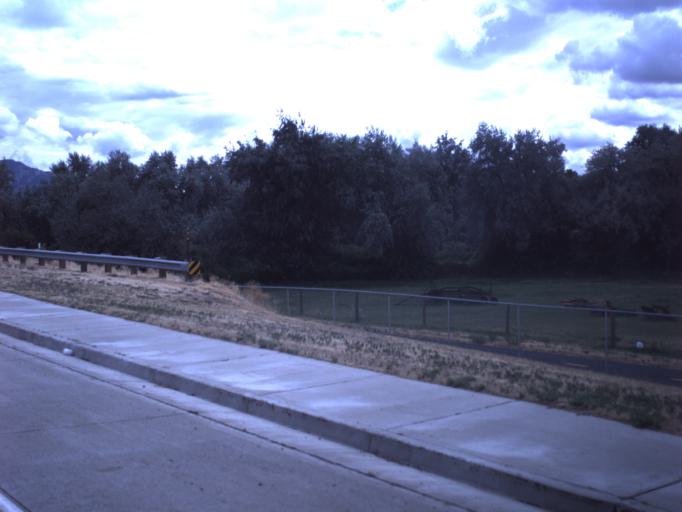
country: US
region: Utah
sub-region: Weber County
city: West Haven
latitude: 41.1975
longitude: -112.0341
